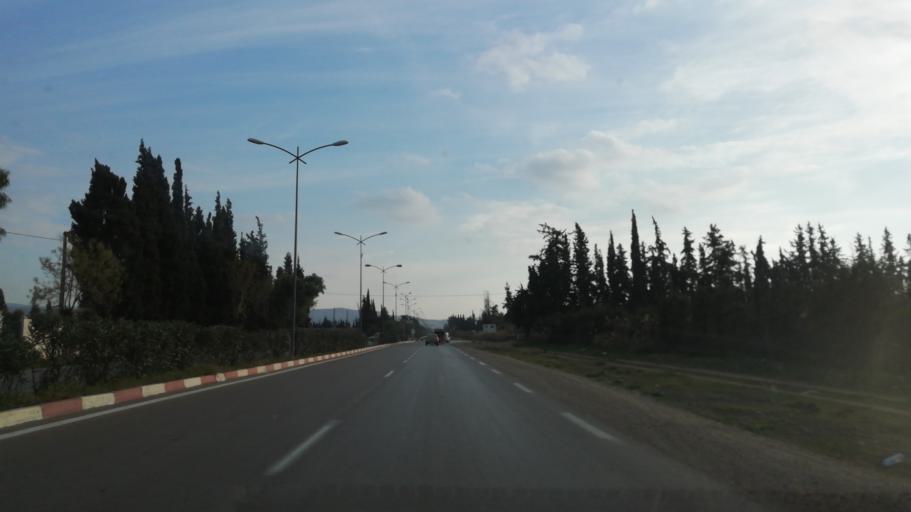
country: DZ
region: Mascara
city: Mascara
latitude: 35.6142
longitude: 0.0626
